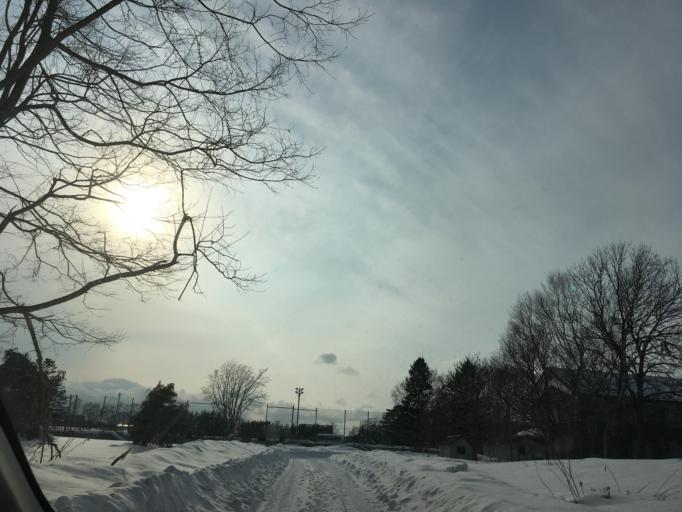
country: JP
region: Hokkaido
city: Ebetsu
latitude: 43.0771
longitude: 141.5164
